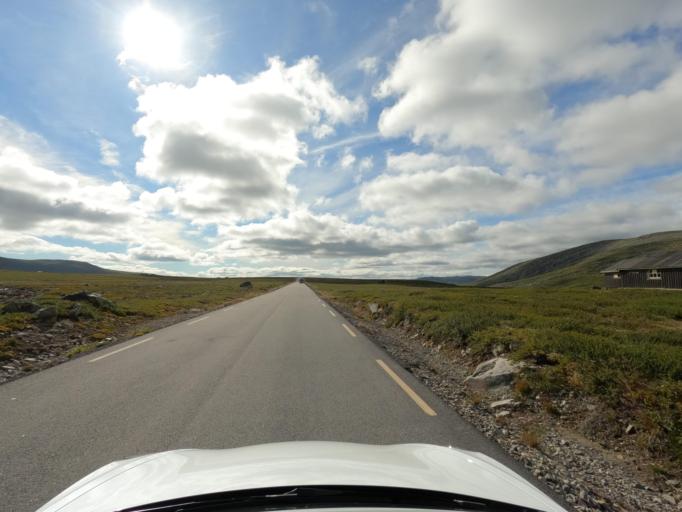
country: NO
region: Telemark
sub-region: Tinn
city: Rjukan
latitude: 60.1742
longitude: 8.5906
